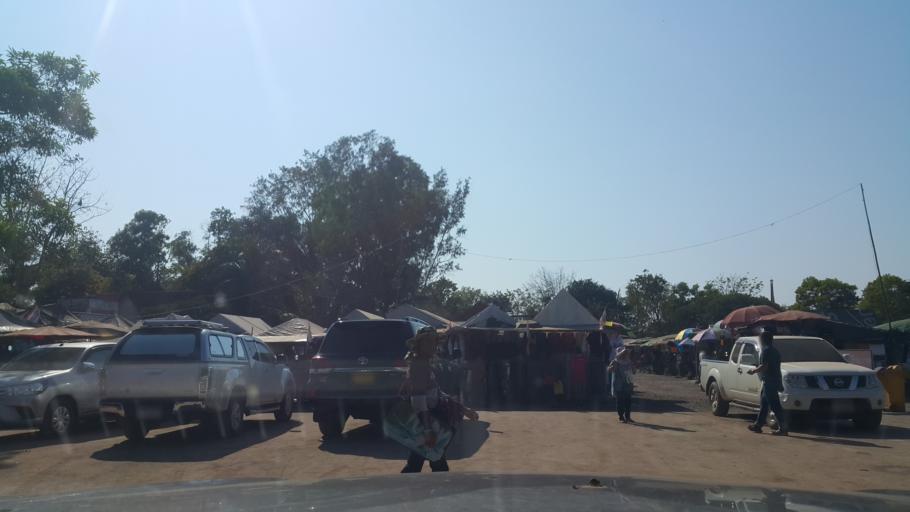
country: TH
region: Changwat Udon Thani
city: Ban Dung
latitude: 17.7445
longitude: 103.3593
